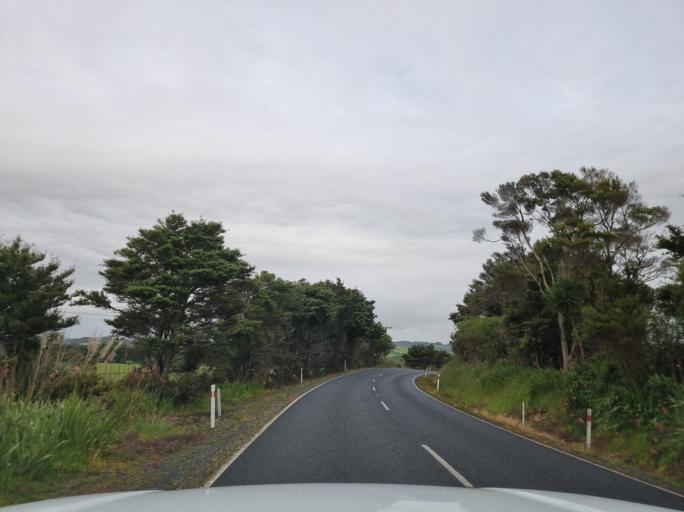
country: NZ
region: Northland
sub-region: Whangarei
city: Ruakaka
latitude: -35.9660
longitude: 174.4205
